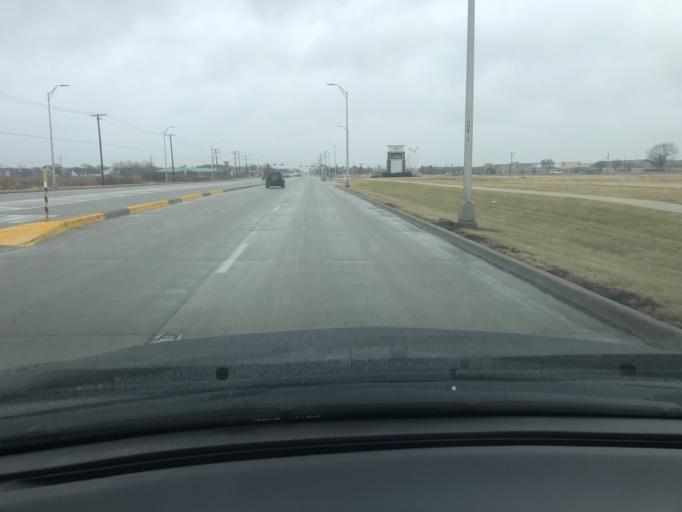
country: US
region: Illinois
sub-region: Will County
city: Shorewood
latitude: 41.5536
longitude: -88.2001
